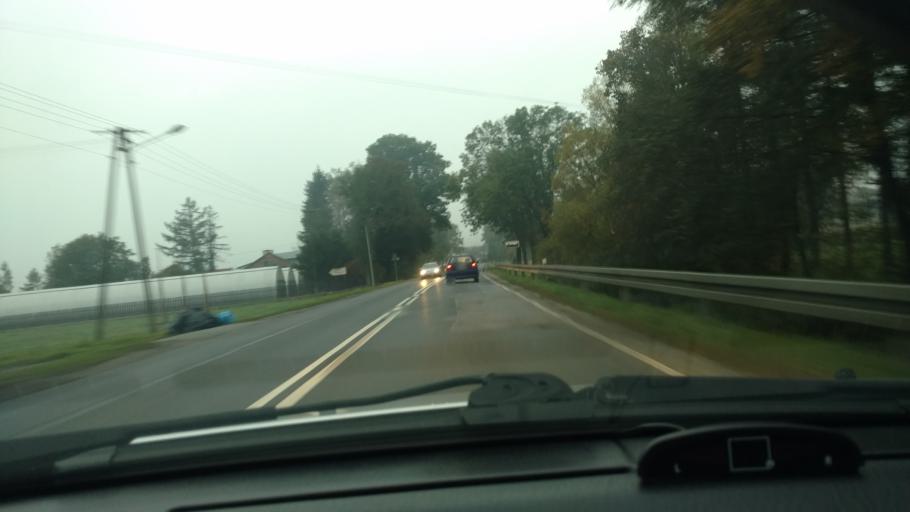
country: PL
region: Subcarpathian Voivodeship
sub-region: Powiat strzyzowski
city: Strzyzow
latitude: 49.8747
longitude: 21.7612
